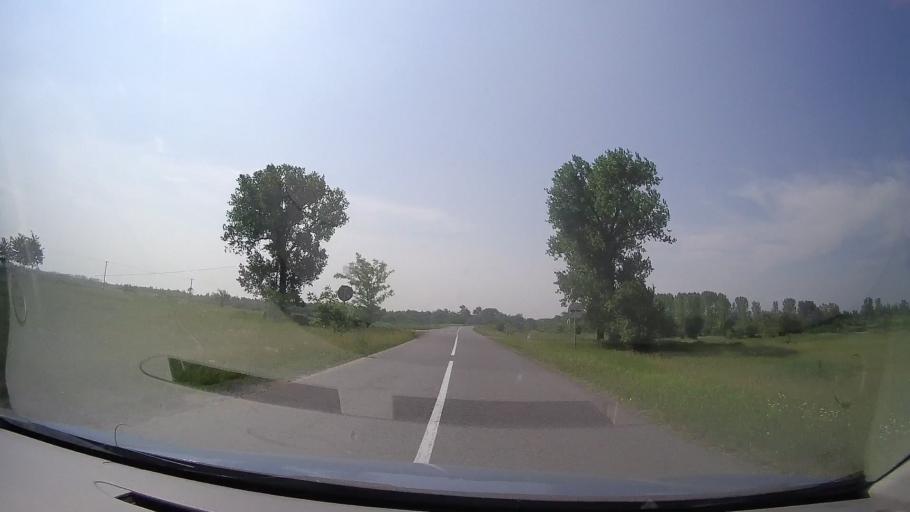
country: RS
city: Jarkovac
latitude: 45.2770
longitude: 20.7633
